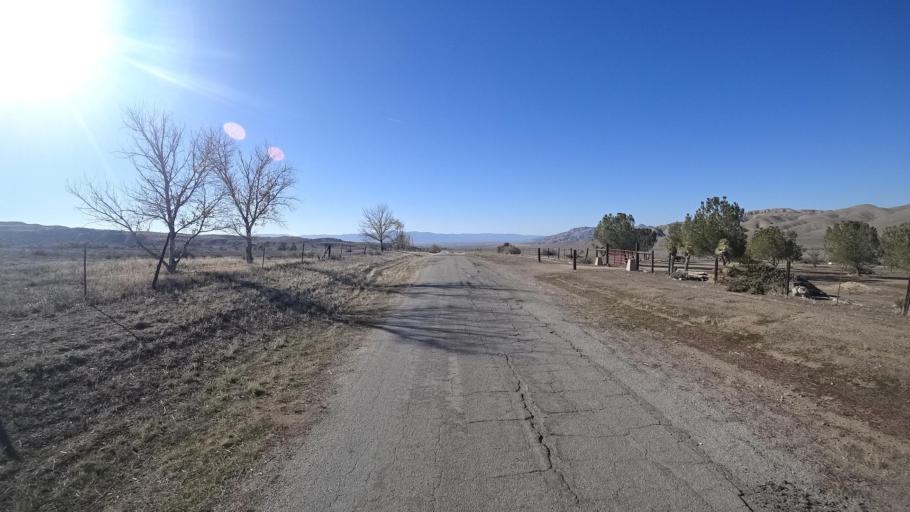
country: US
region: California
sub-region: Kern County
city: Maricopa
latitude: 34.9383
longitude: -119.4606
